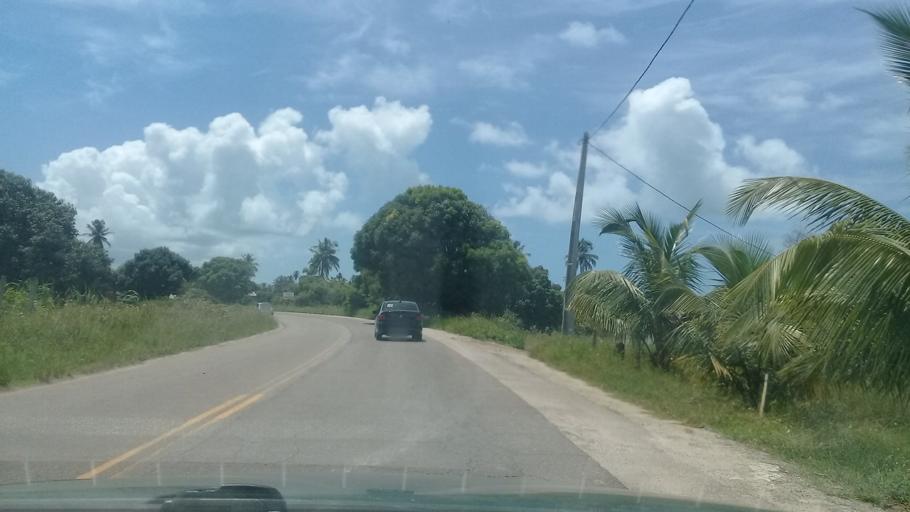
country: BR
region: Pernambuco
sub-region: Sirinhaem
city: Sirinhaem
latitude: -8.6259
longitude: -35.0661
